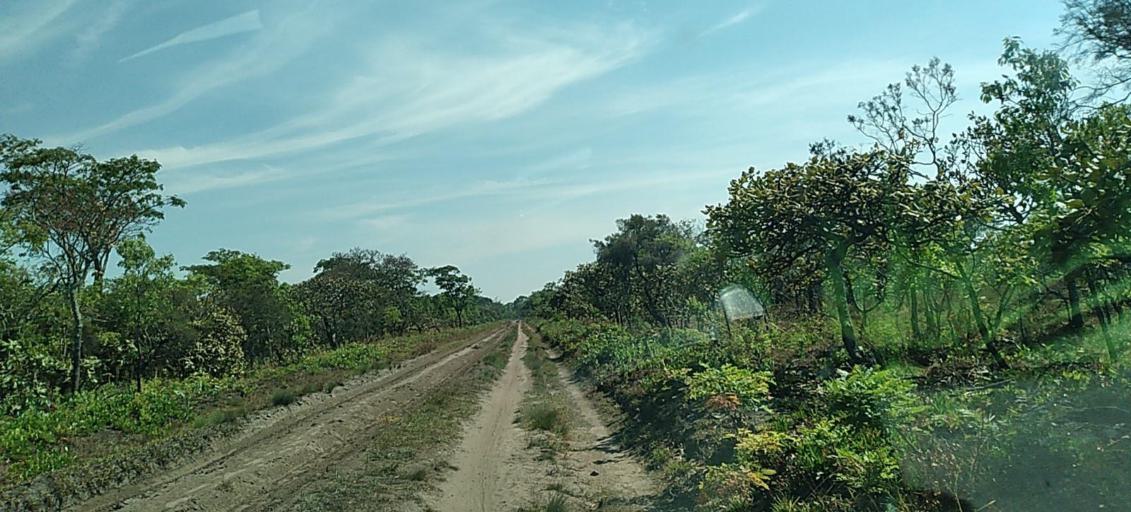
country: ZM
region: North-Western
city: Mwinilunga
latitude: -11.8014
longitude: 25.1661
